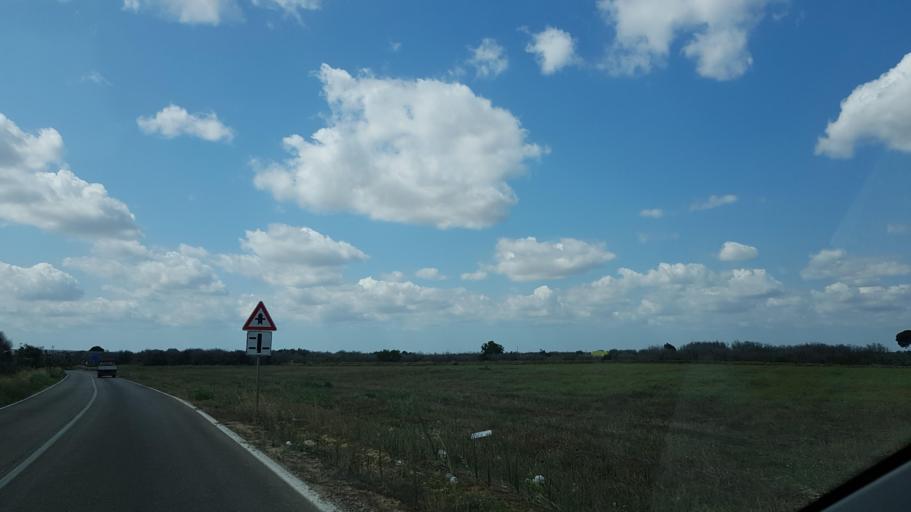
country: IT
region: Apulia
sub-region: Provincia di Brindisi
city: Torchiarolo
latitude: 40.4665
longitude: 18.0593
